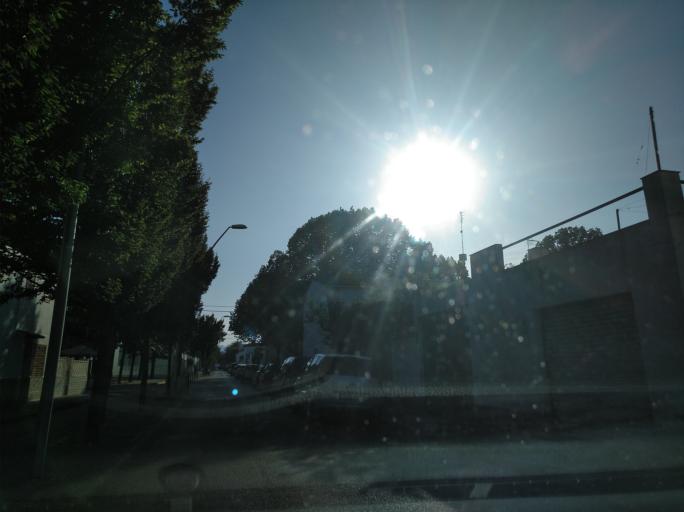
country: ES
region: Catalonia
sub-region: Provincia de Girona
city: Salt
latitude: 41.9716
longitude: 2.7890
